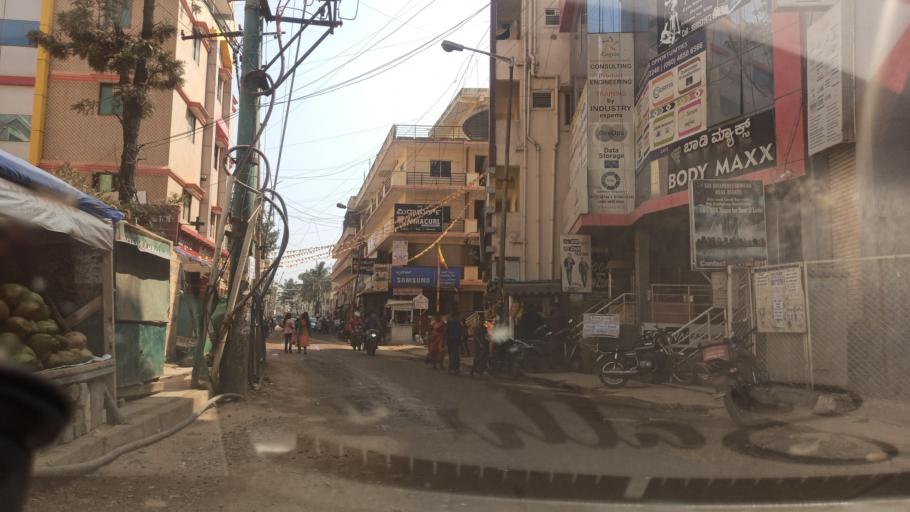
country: IN
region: Karnataka
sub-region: Bangalore Urban
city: Bangalore
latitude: 12.9483
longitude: 77.7044
